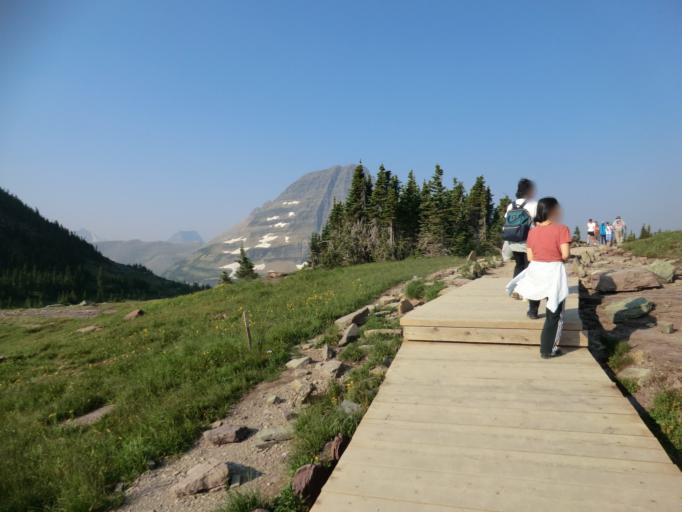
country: US
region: Montana
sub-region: Flathead County
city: Columbia Falls
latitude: 48.6877
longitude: -113.7380
